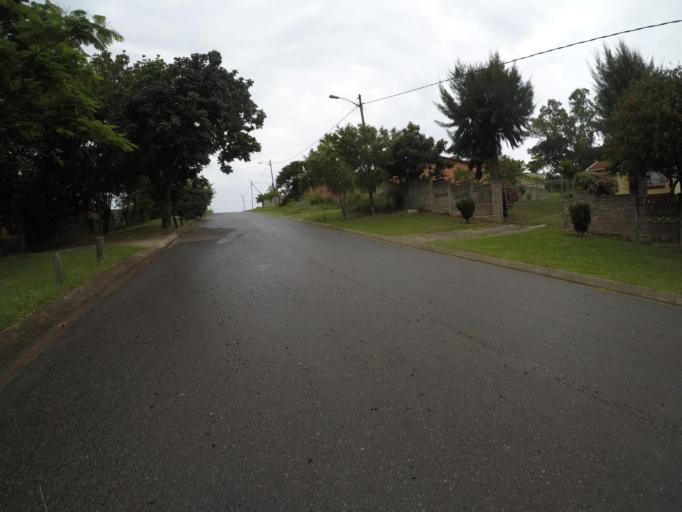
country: ZA
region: Eastern Cape
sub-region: Buffalo City Metropolitan Municipality
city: East London
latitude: -32.9634
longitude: 27.8480
